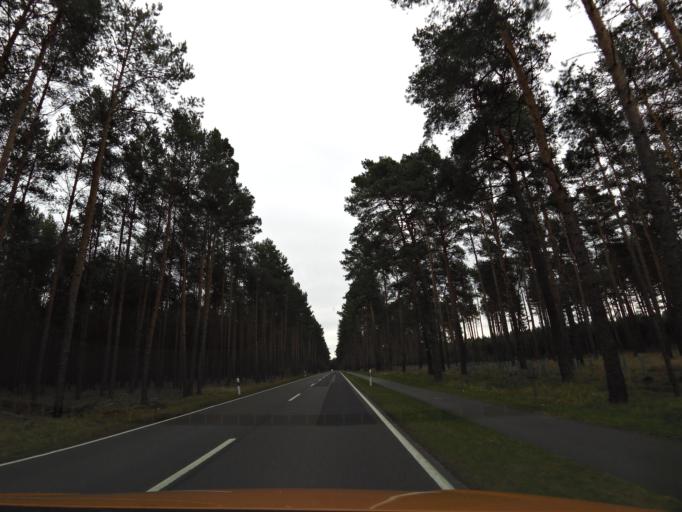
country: DE
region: Brandenburg
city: Borkheide
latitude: 52.2027
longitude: 12.8419
